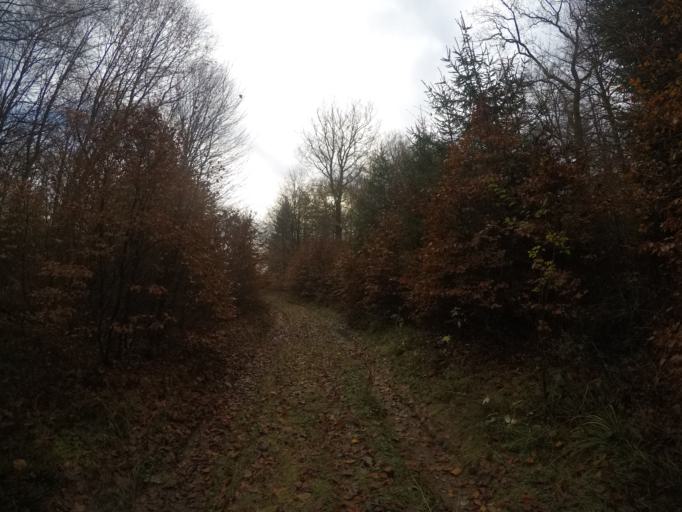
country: BE
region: Wallonia
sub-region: Province du Luxembourg
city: Habay-la-Vieille
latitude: 49.7420
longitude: 5.6007
